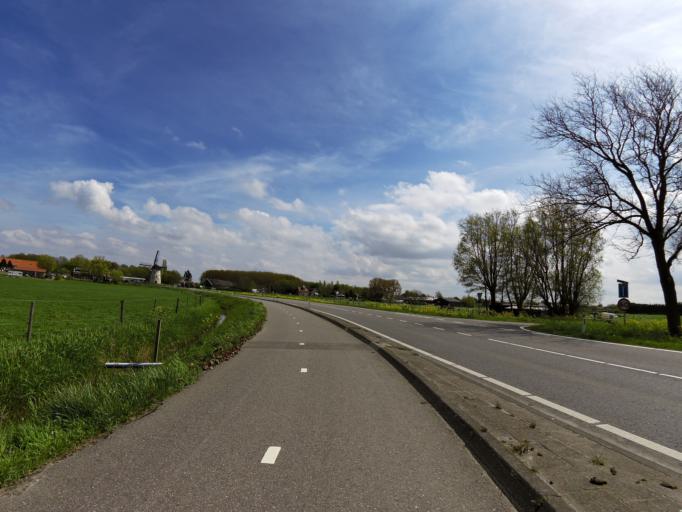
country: NL
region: South Holland
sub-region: Gemeente Hellevoetsluis
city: Nieuwenhoorn
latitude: 51.8490
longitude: 4.1355
